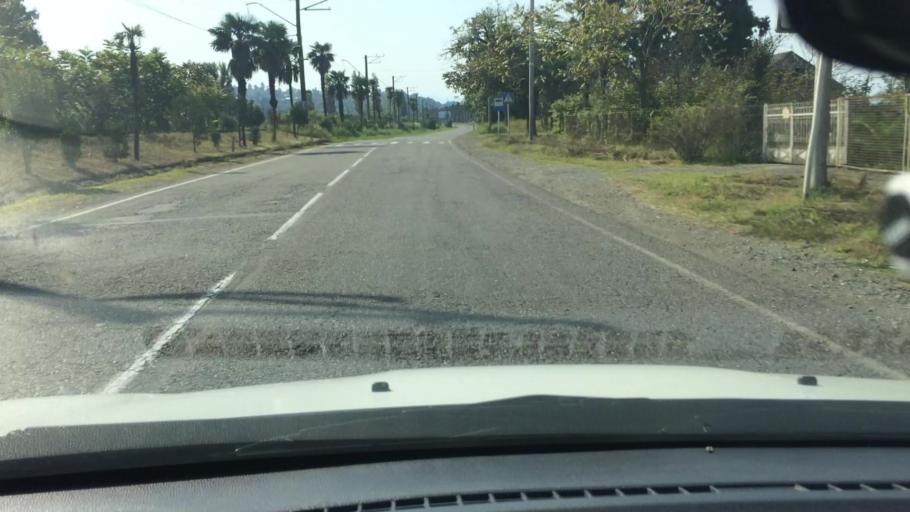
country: GE
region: Ajaria
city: Kobuleti
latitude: 41.7946
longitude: 41.7707
